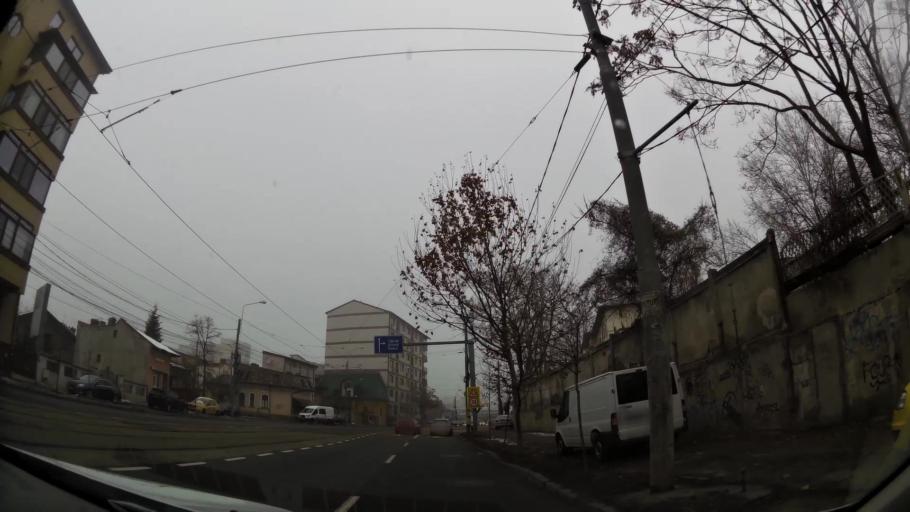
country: RO
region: Bucuresti
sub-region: Municipiul Bucuresti
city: Bucuresti
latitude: 44.4521
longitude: 26.0586
